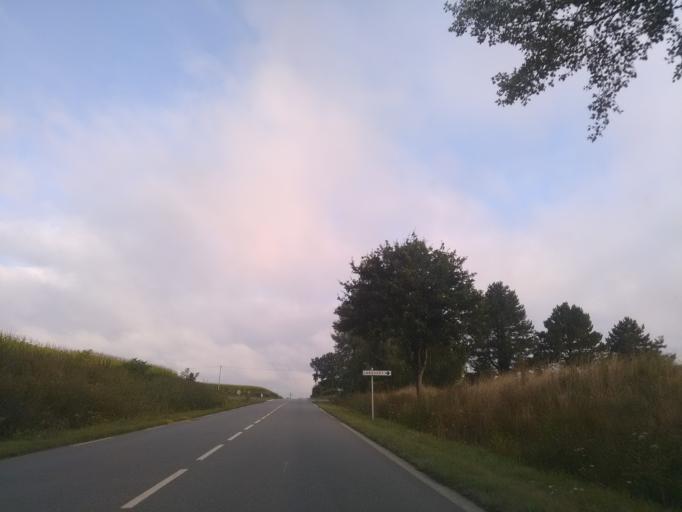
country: FR
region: Brittany
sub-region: Departement d'Ille-et-Vilaine
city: Vignoc
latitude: 48.2472
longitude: -1.8223
